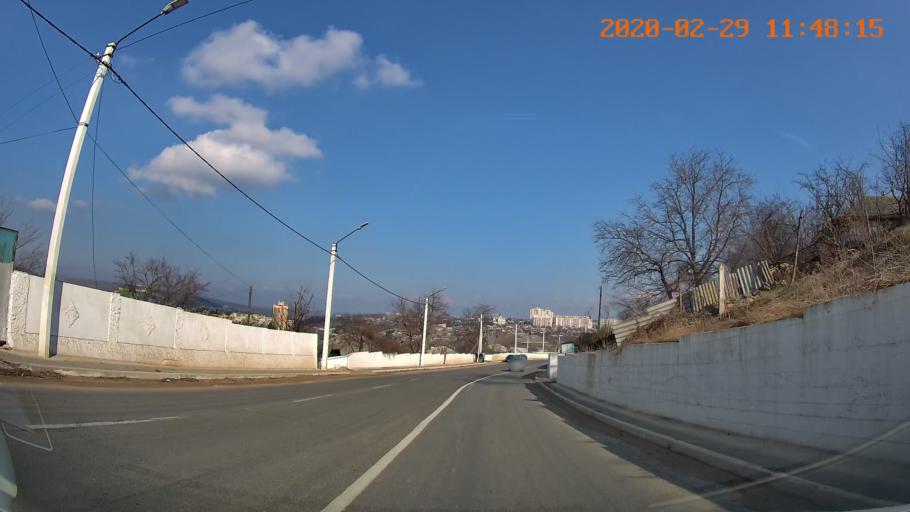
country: MD
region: Rezina
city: Rezina
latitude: 47.7471
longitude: 28.9894
